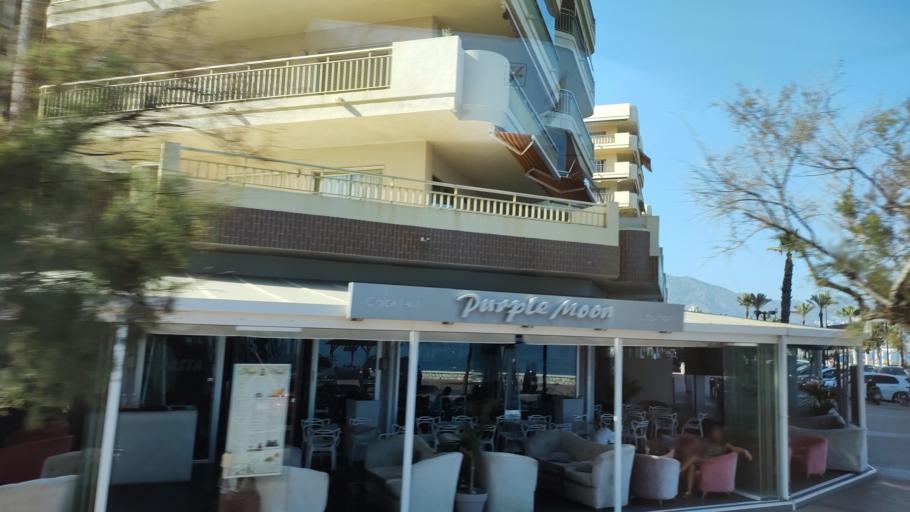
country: ES
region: Andalusia
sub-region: Provincia de Malaga
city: Fuengirola
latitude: 36.5287
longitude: -4.6258
